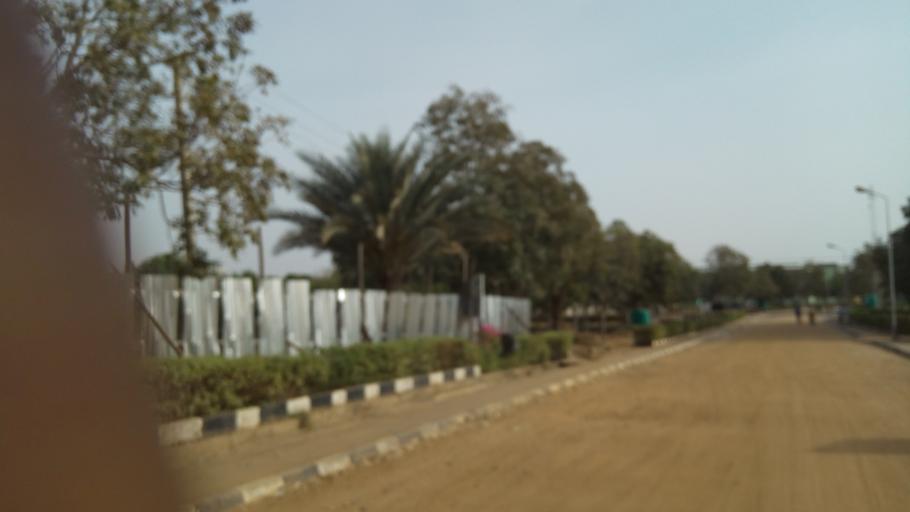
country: NG
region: Gombe
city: Gombe
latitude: 10.3071
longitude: 11.1750
